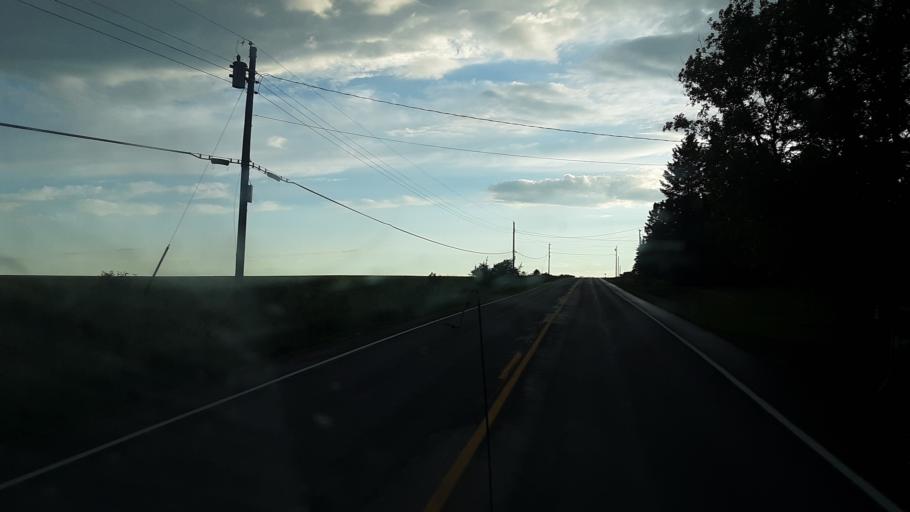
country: US
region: Maine
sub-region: Aroostook County
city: Easton
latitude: 46.6754
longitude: -67.9549
